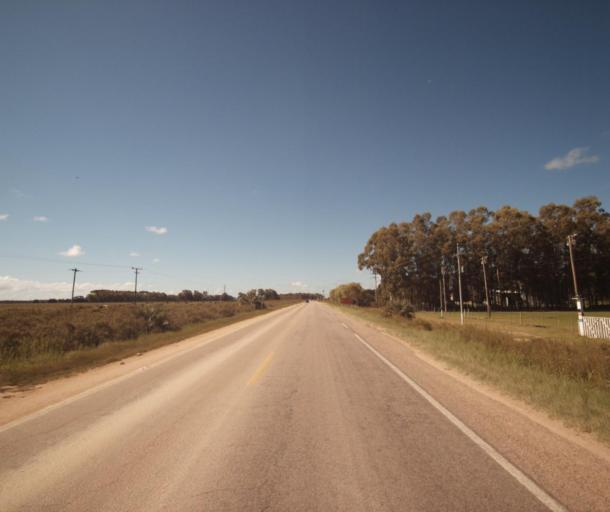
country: BR
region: Rio Grande do Sul
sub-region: Santa Vitoria Do Palmar
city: Santa Vitoria do Palmar
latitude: -33.5637
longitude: -53.3724
